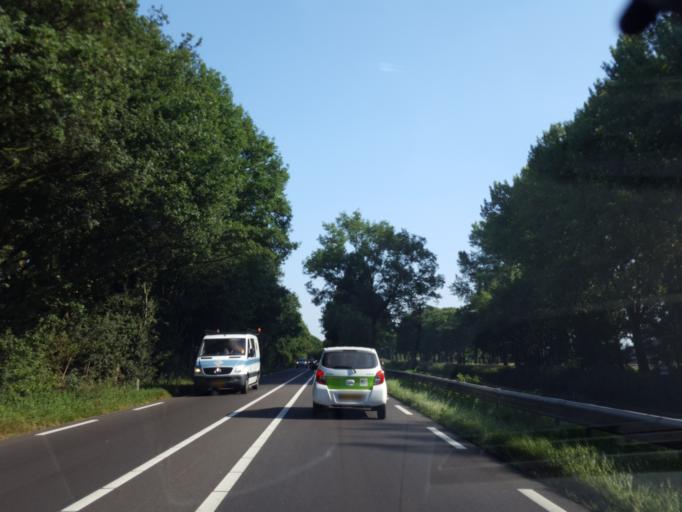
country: NL
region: North Brabant
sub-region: Gemeente Veghel
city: Keldonk
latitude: 51.5557
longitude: 5.6126
